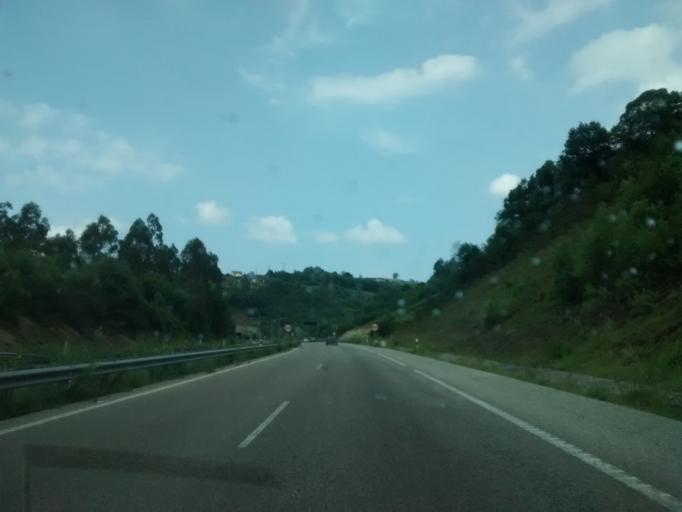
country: ES
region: Asturias
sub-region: Province of Asturias
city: Mieres
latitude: 43.2817
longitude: -5.7616
